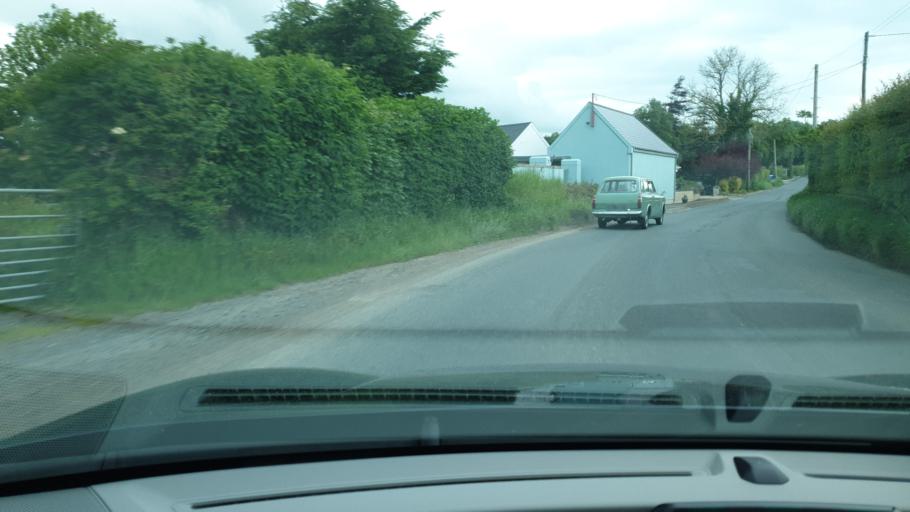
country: IE
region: Leinster
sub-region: An Mhi
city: Ashbourne
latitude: 53.5422
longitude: -6.4115
